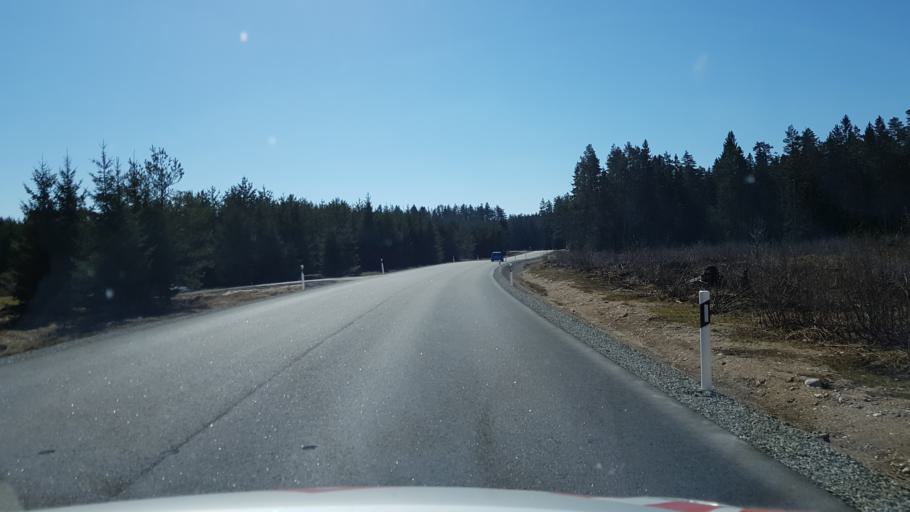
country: EE
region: Laeaene-Virumaa
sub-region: Vinni vald
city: Vinni
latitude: 59.1408
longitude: 26.5971
